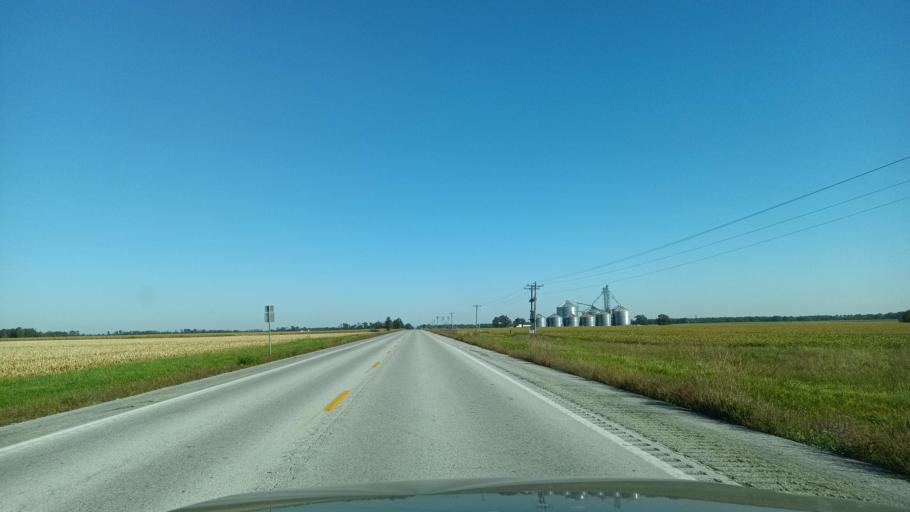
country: US
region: Missouri
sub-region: Audrain County
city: Vandalia
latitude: 39.3629
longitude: -91.6424
